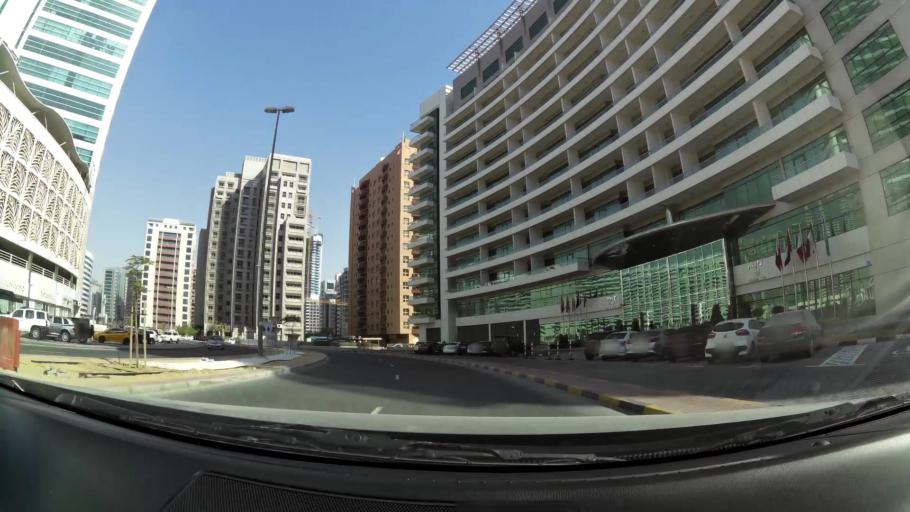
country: AE
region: Dubai
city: Dubai
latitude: 25.0969
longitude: 55.1729
